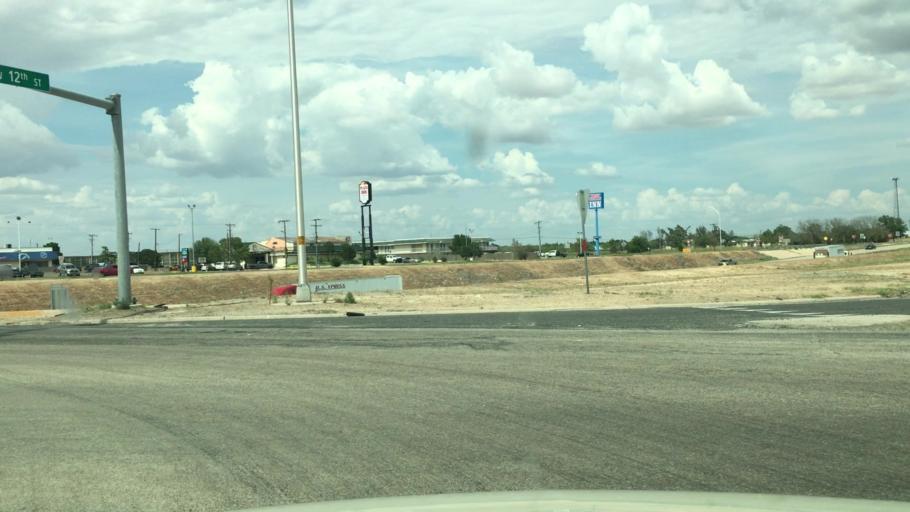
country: US
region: Texas
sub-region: Howard County
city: Big Spring
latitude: 32.2630
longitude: -101.4901
